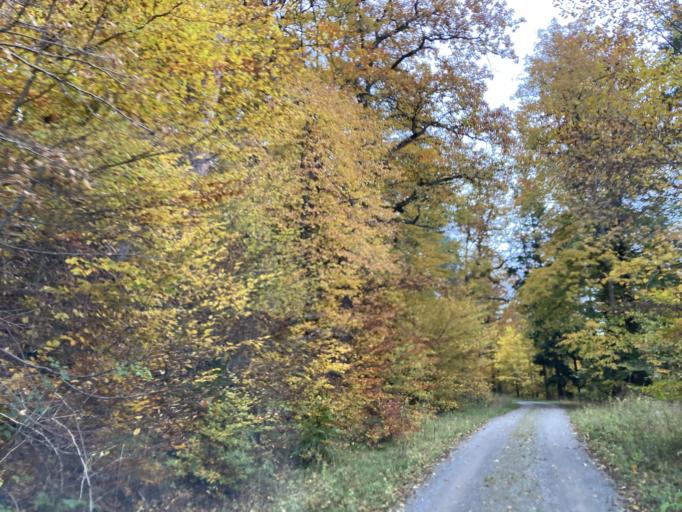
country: DE
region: Baden-Wuerttemberg
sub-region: Tuebingen Region
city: Dusslingen
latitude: 48.4652
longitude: 9.0018
